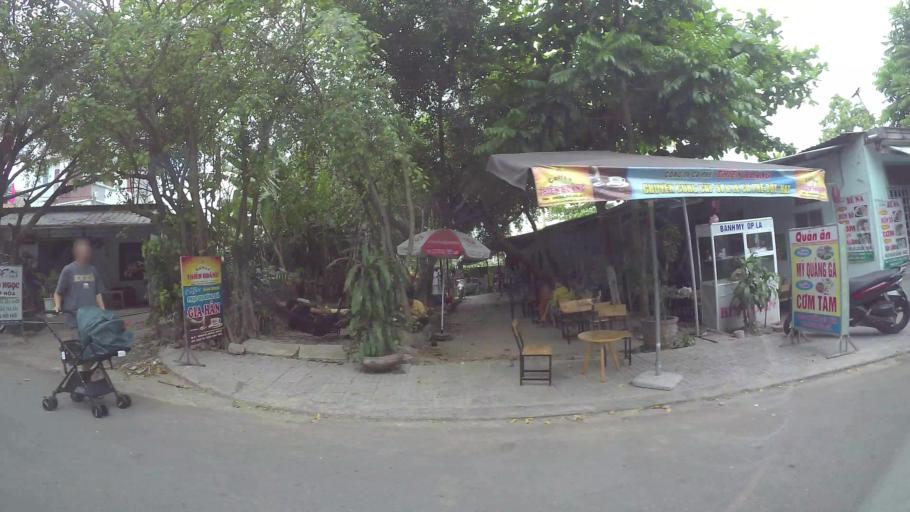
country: VN
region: Da Nang
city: Thanh Khe
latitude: 16.0680
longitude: 108.1847
